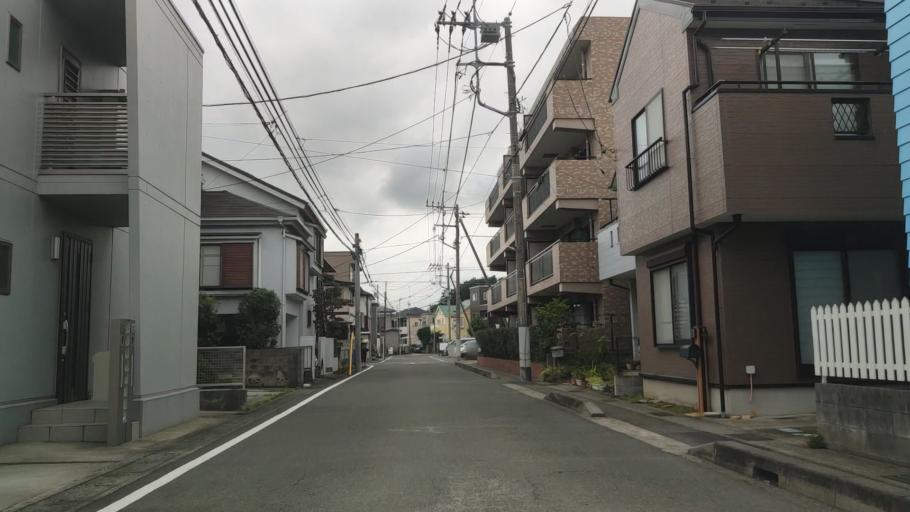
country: JP
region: Kanagawa
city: Minami-rinkan
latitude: 35.5023
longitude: 139.4419
